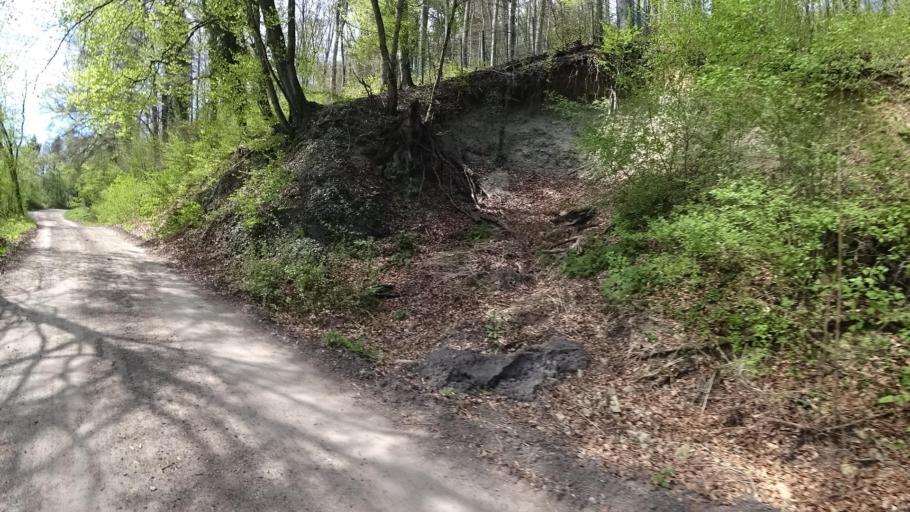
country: DE
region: Rheinland-Pfalz
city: Ralingen
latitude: 49.8214
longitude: 6.5251
